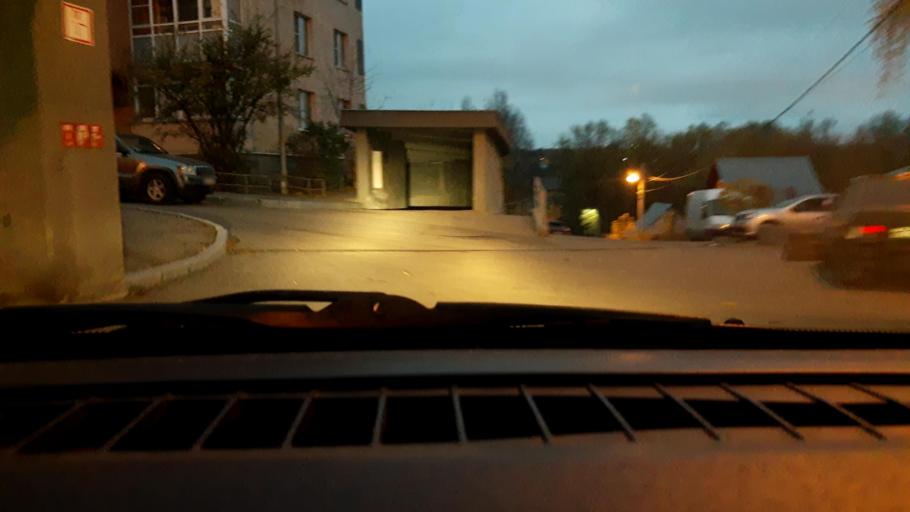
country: RU
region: Nizjnij Novgorod
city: Nizhniy Novgorod
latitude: 56.3012
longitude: 44.0240
